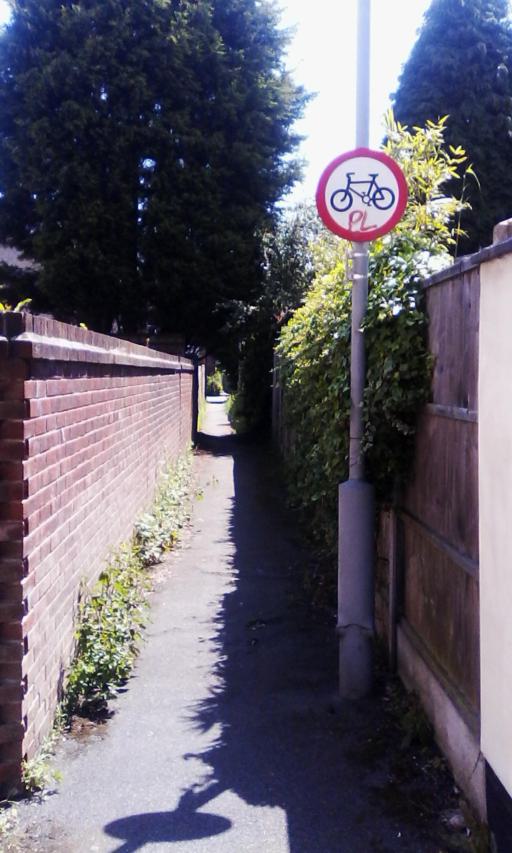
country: GB
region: England
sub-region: Nottinghamshire
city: Arnold
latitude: 52.9744
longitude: -1.1197
